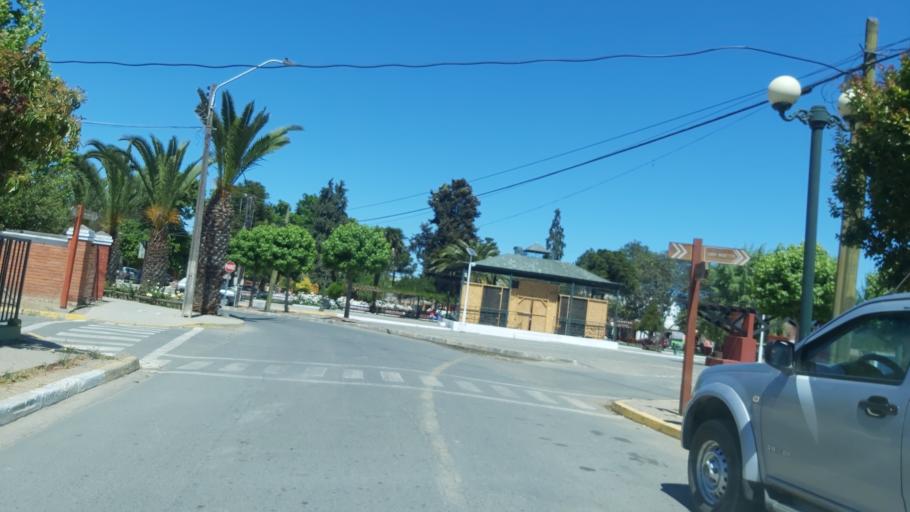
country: CL
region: Maule
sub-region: Provincia de Talca
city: Talca
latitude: -34.9853
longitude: -71.9837
